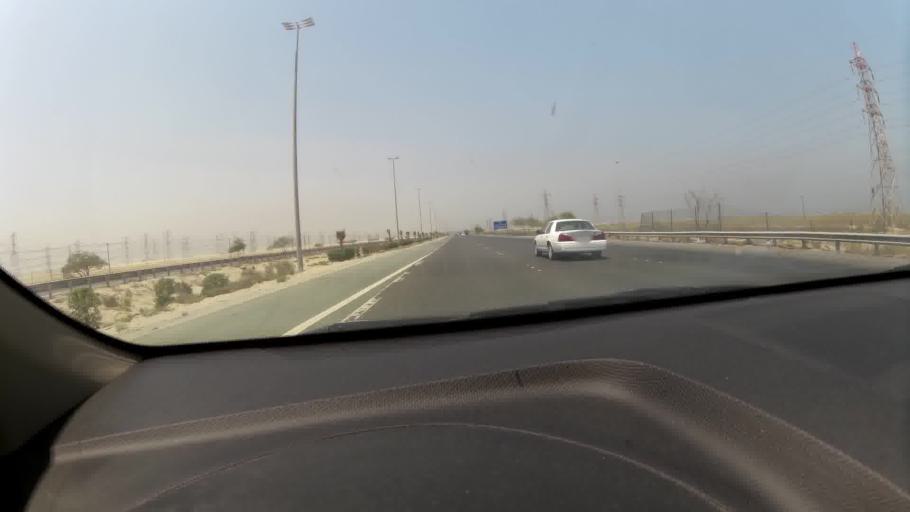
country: KW
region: Al Ahmadi
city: Al Fahahil
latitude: 28.8462
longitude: 48.2470
